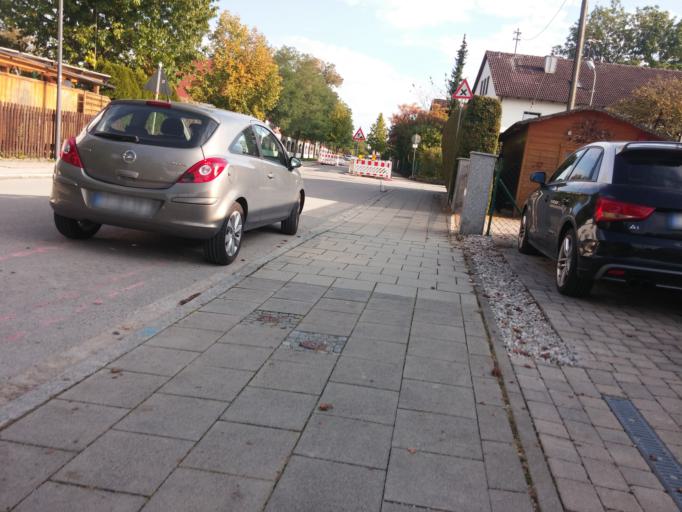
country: DE
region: Bavaria
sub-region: Upper Bavaria
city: Feldkirchen
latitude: 48.1460
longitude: 11.7353
